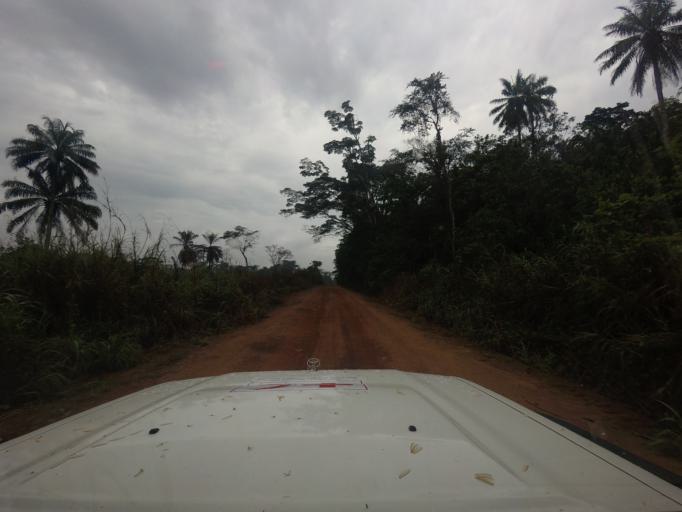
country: LR
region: Lofa
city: Voinjama
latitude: 8.3917
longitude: -9.8102
